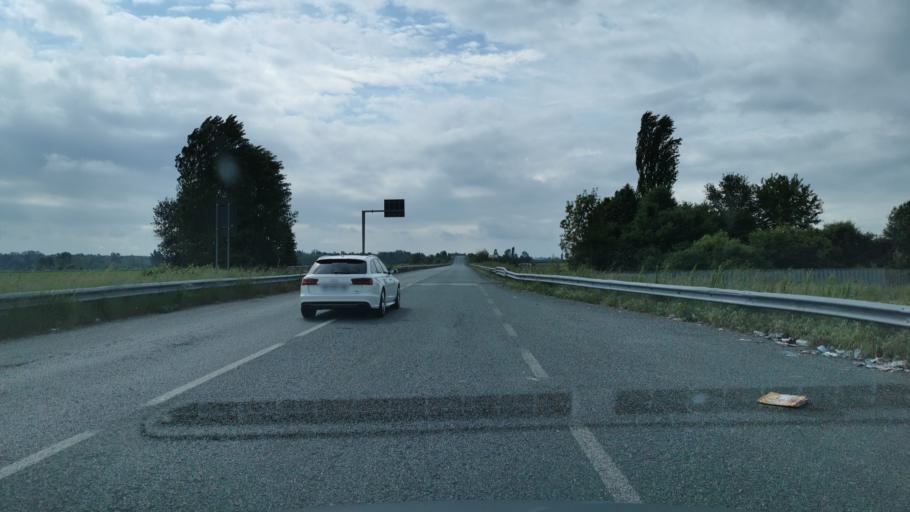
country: IT
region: Piedmont
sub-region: Provincia di Cuneo
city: Racconigi
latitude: 44.7999
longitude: 7.6931
